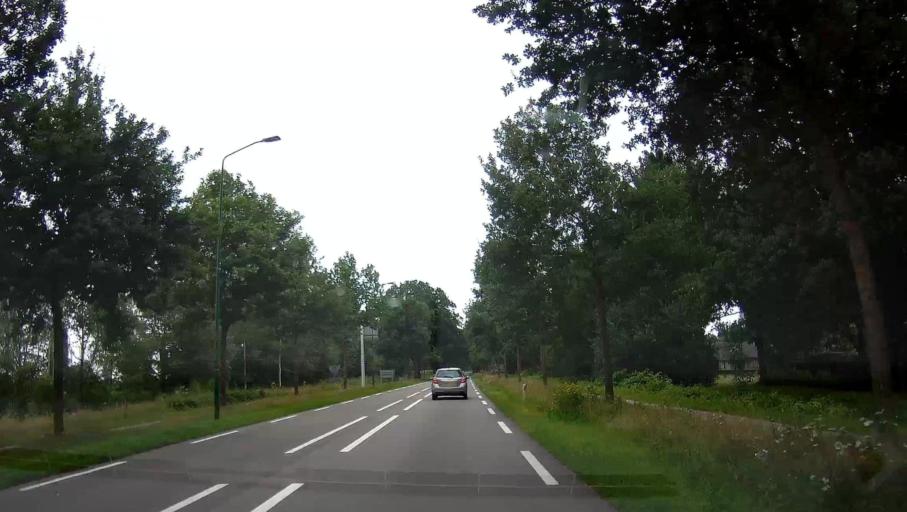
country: NL
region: North Brabant
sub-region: Gemeente Bladel en Netersel
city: Bladel
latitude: 51.4055
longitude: 5.1534
